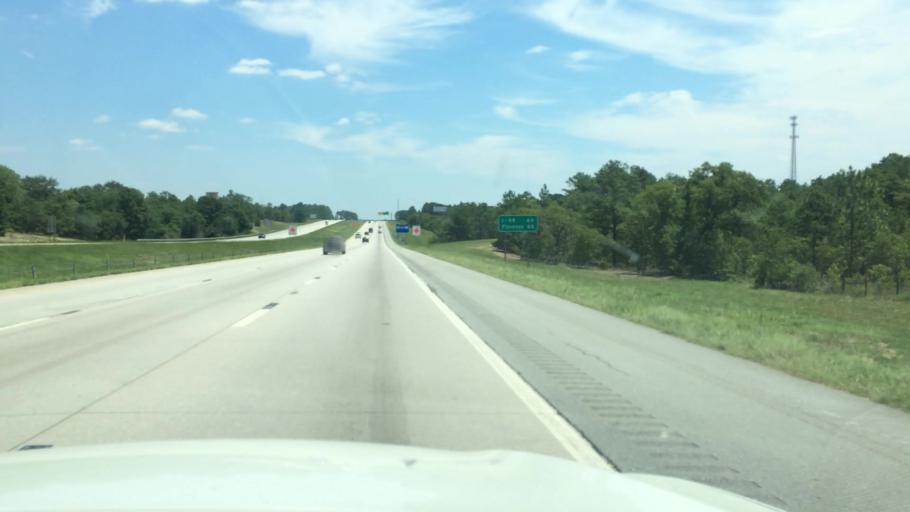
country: US
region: South Carolina
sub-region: Kershaw County
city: Elgin
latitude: 34.1001
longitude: -80.8418
